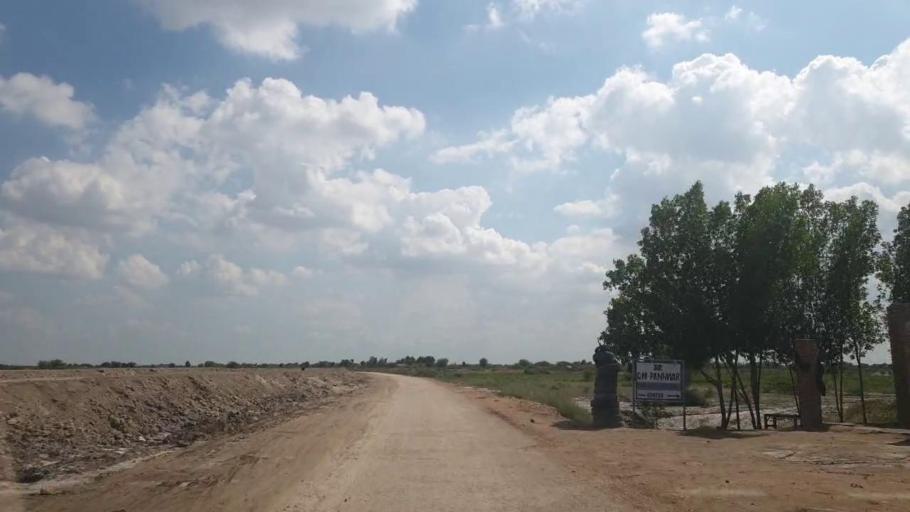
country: PK
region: Sindh
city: Pithoro
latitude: 25.5894
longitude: 69.3940
